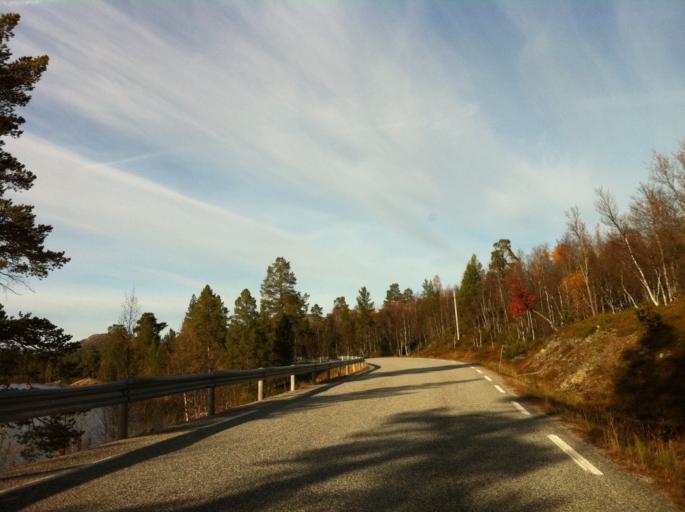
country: NO
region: Hedmark
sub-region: Engerdal
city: Engerdal
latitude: 62.0993
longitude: 12.0296
